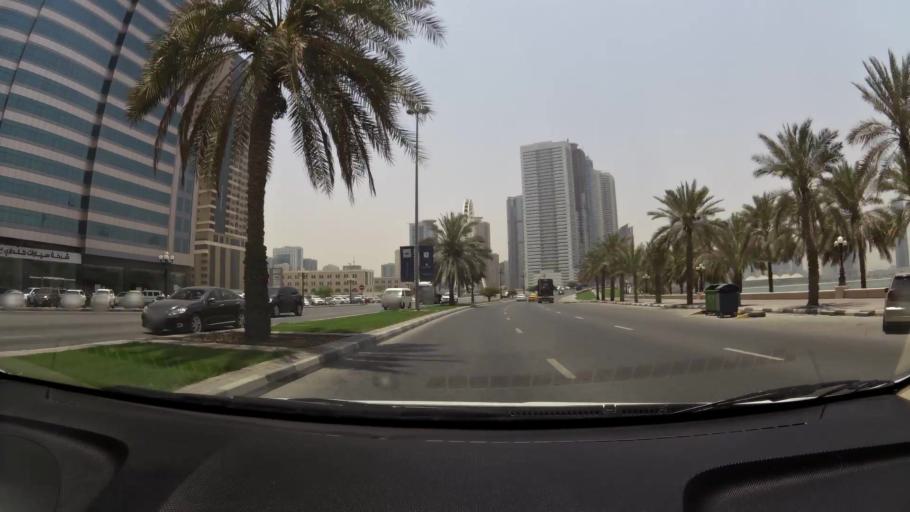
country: AE
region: Ash Shariqah
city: Sharjah
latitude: 25.3241
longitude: 55.3739
